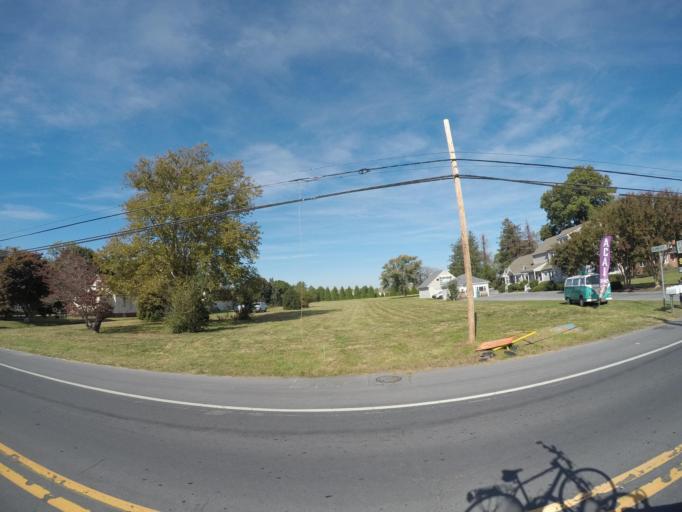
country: US
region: Delaware
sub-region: Sussex County
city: Lewes
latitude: 38.7541
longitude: -75.1607
